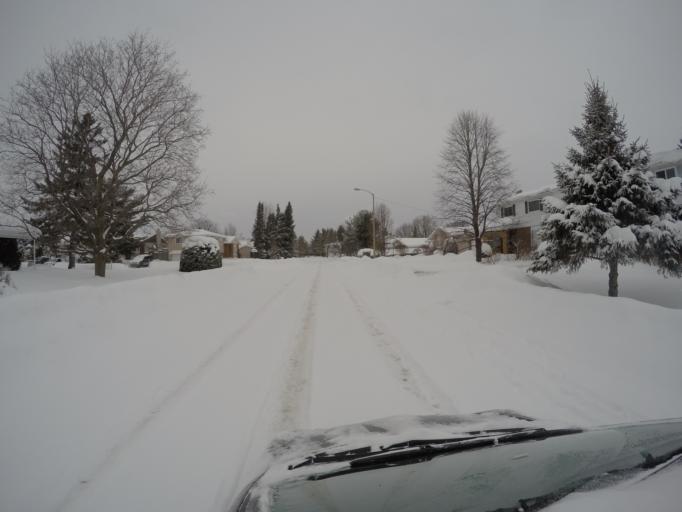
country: CA
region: Quebec
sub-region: Outaouais
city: Gatineau
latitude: 45.4711
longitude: -75.4948
